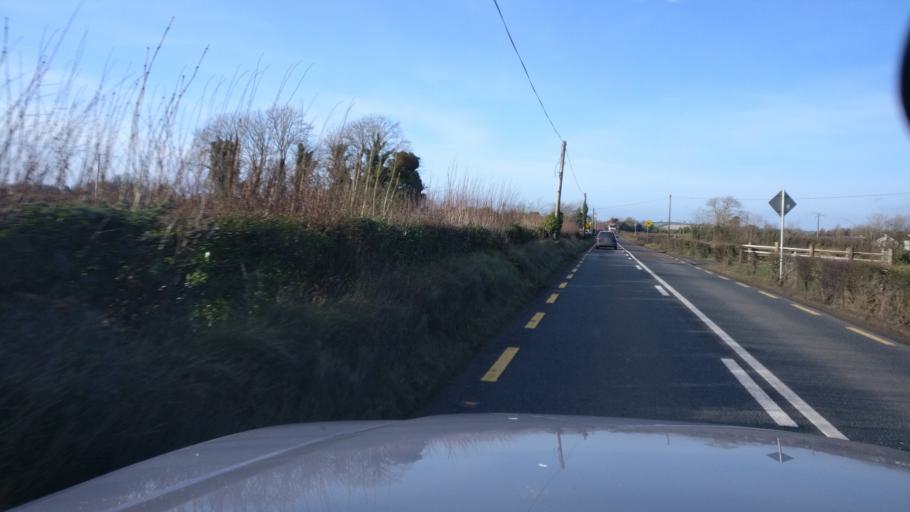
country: IE
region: Leinster
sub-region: Laois
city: Mountmellick
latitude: 53.1706
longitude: -7.3806
